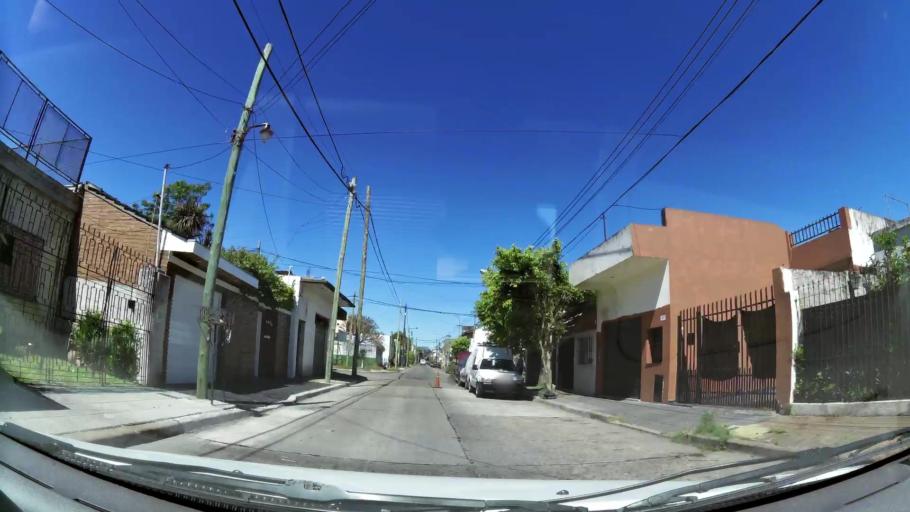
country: AR
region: Buenos Aires
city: Caseros
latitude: -34.5902
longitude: -58.5484
